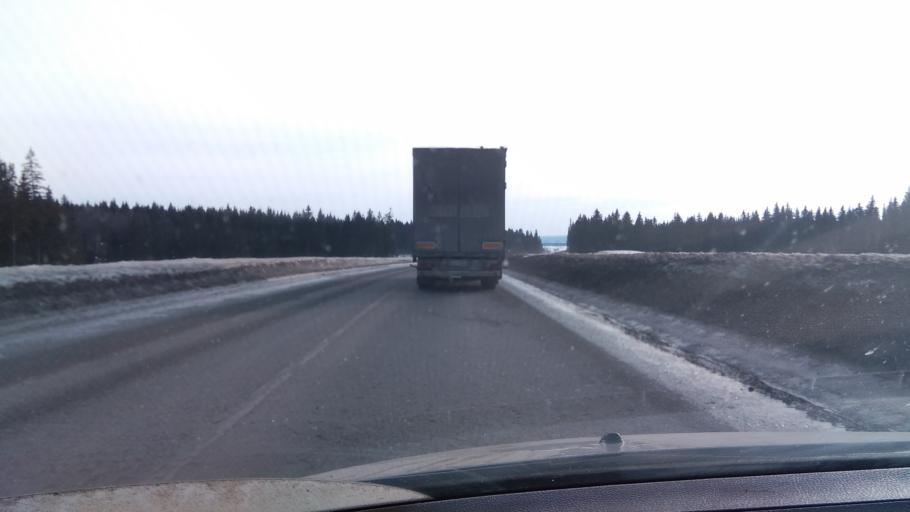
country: RU
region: Perm
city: Ferma
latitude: 57.9502
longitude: 56.3887
